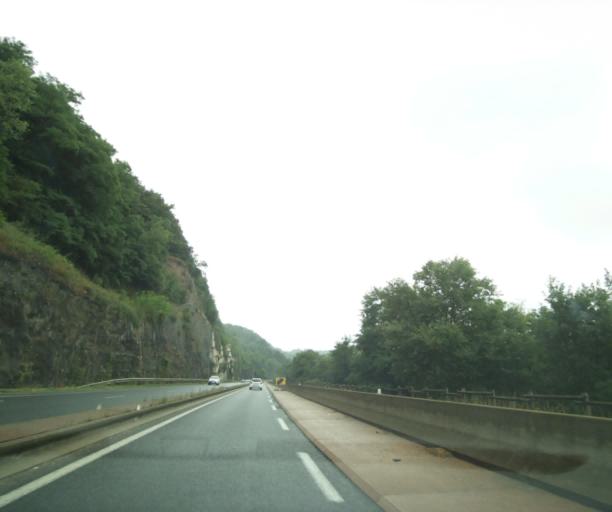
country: FR
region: Midi-Pyrenees
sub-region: Departement de l'Aveyron
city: Olemps
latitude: 44.3476
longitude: 2.5566
